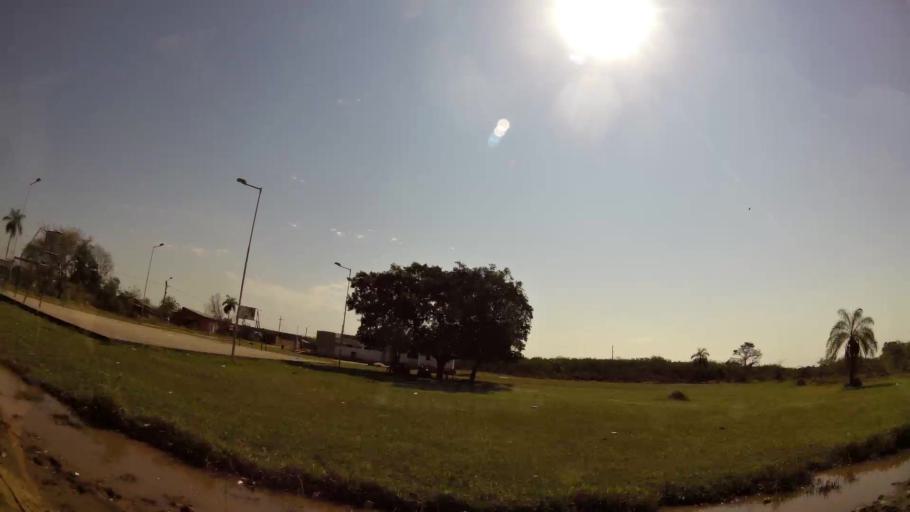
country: BO
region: Santa Cruz
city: Cotoca
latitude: -17.7122
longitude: -63.0633
